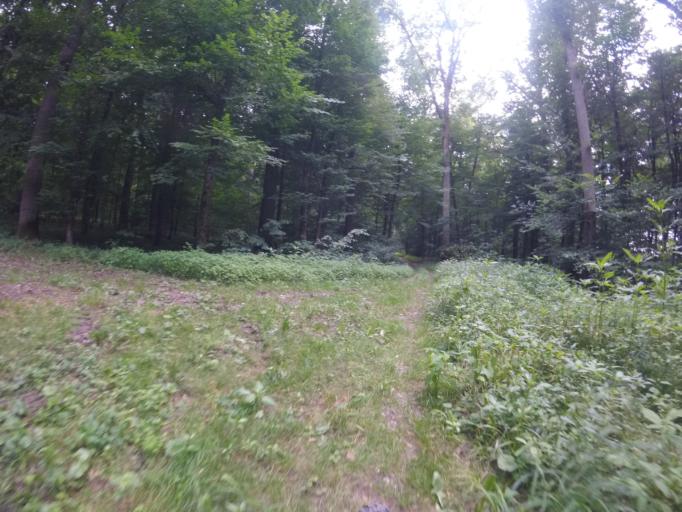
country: DE
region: Baden-Wuerttemberg
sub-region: Regierungsbezirk Stuttgart
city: Backnang
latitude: 48.9664
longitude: 9.4370
